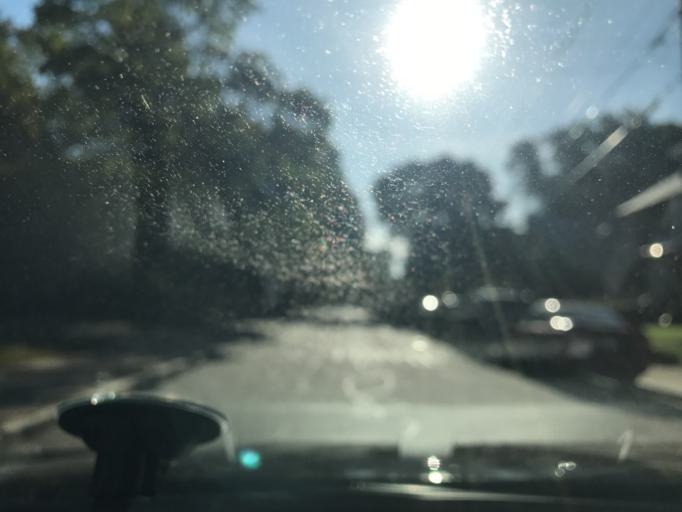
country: US
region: Massachusetts
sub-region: Suffolk County
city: Jamaica Plain
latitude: 42.3184
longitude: -71.1160
